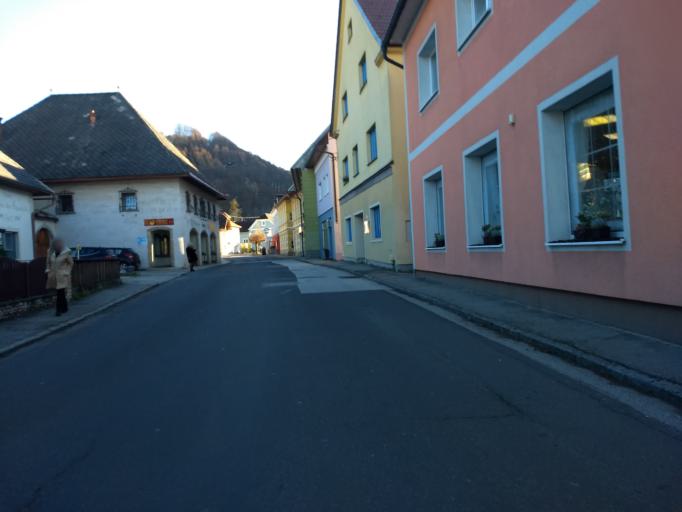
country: AT
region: Upper Austria
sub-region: Politischer Bezirk Kirchdorf an der Krems
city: Micheldorf in Oberoesterreich
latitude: 47.8782
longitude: 14.1332
